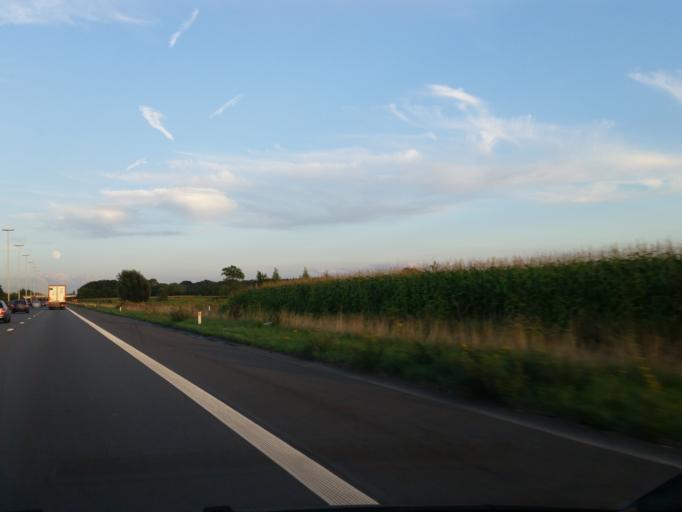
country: BE
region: Flanders
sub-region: Provincie West-Vlaanderen
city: Oostkamp
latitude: 51.1369
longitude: 3.2673
